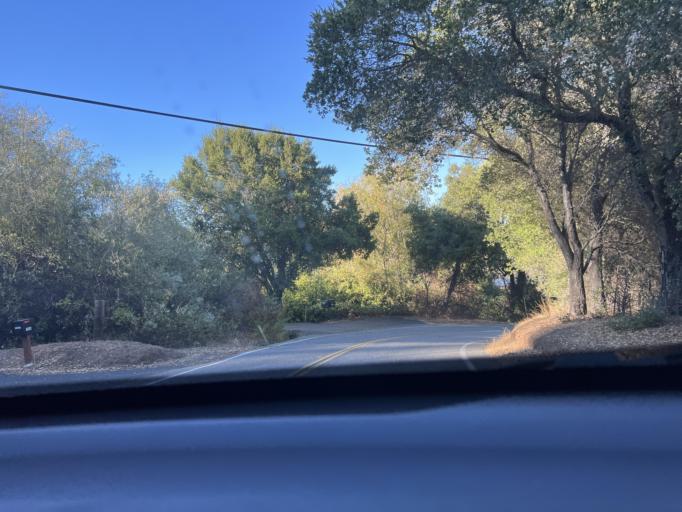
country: US
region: California
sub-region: Santa Clara County
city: Loyola
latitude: 37.2908
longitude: -122.0910
